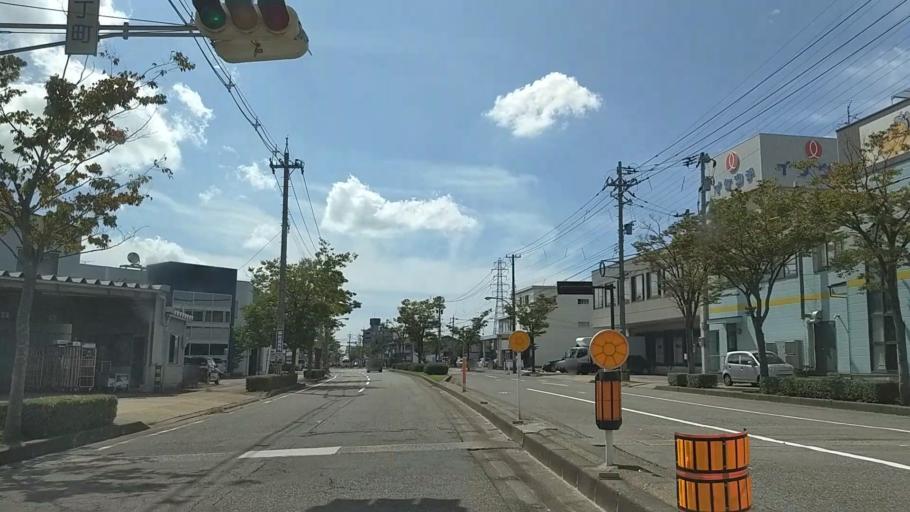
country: JP
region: Ishikawa
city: Kanazawa-shi
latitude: 36.5838
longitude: 136.6349
